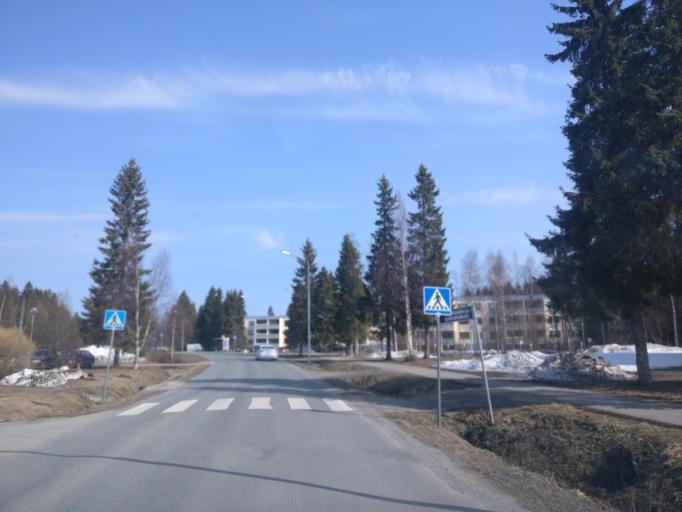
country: FI
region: Lapland
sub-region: Kemi-Tornio
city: Kemi
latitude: 65.7279
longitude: 24.6252
